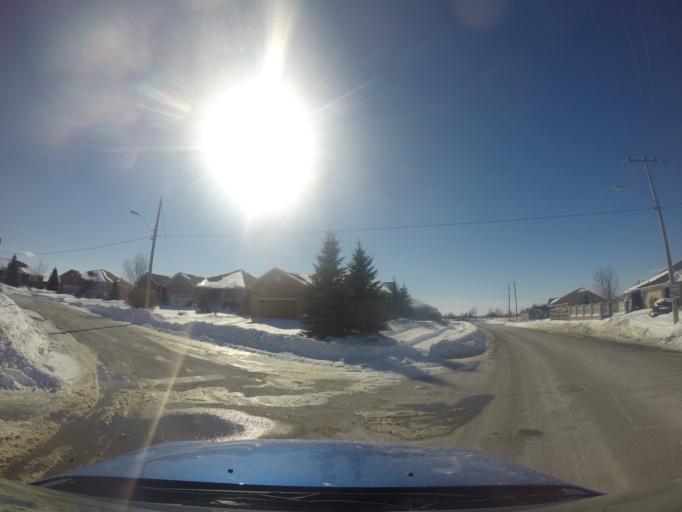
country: CA
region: Ontario
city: Omemee
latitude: 44.3395
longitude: -78.7584
